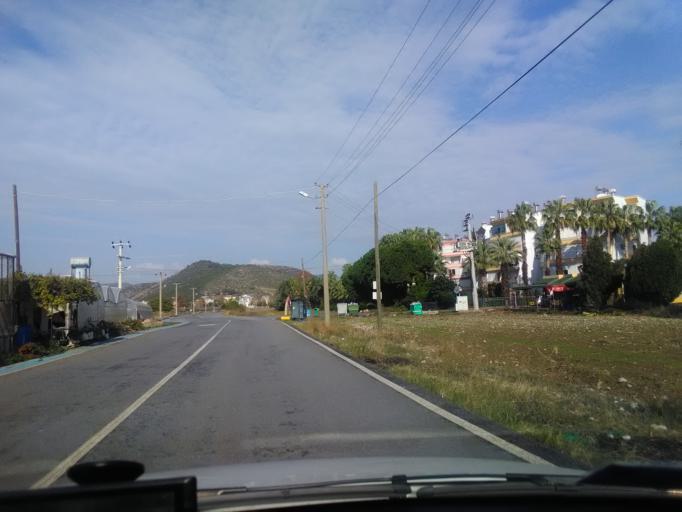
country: TR
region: Antalya
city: Gazipasa
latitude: 36.2557
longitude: 32.2910
